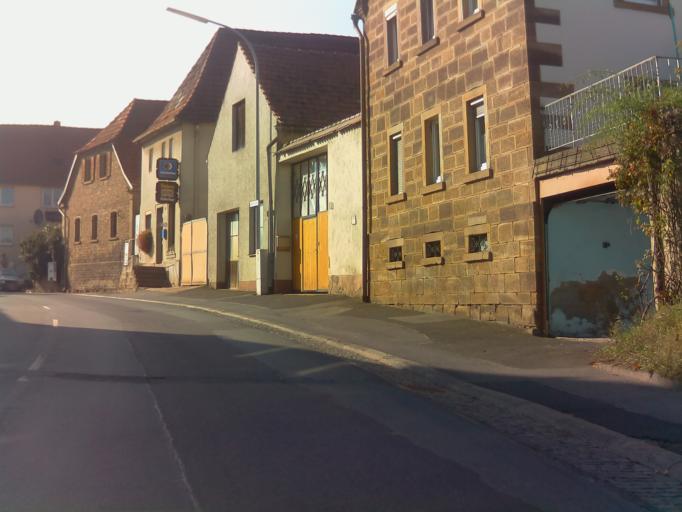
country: DE
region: Bavaria
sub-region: Regierungsbezirk Unterfranken
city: Prichsenstadt
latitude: 49.8366
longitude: 10.3301
